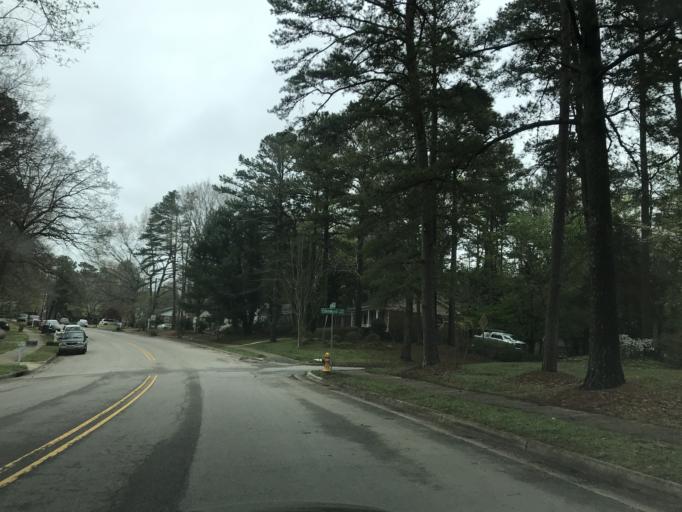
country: US
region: North Carolina
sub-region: Wake County
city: West Raleigh
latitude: 35.8780
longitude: -78.6500
